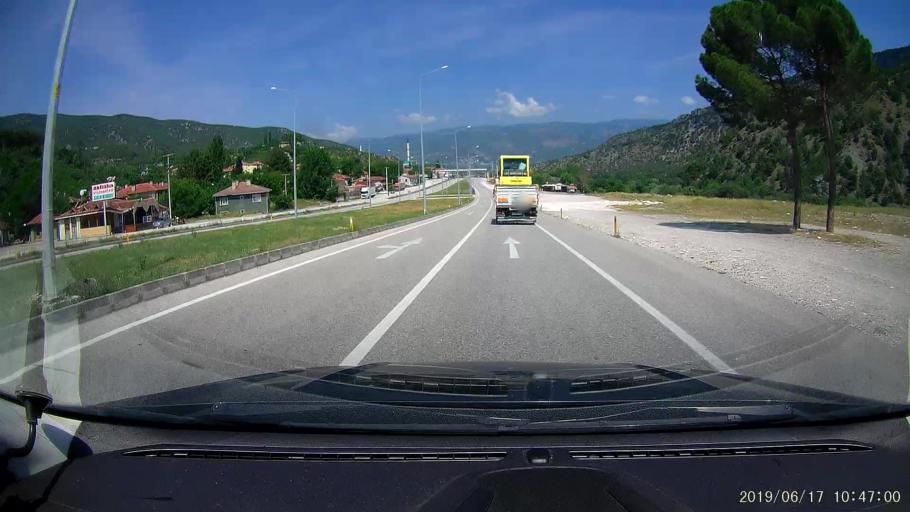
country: TR
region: Corum
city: Hacihamza
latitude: 41.0738
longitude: 34.4541
